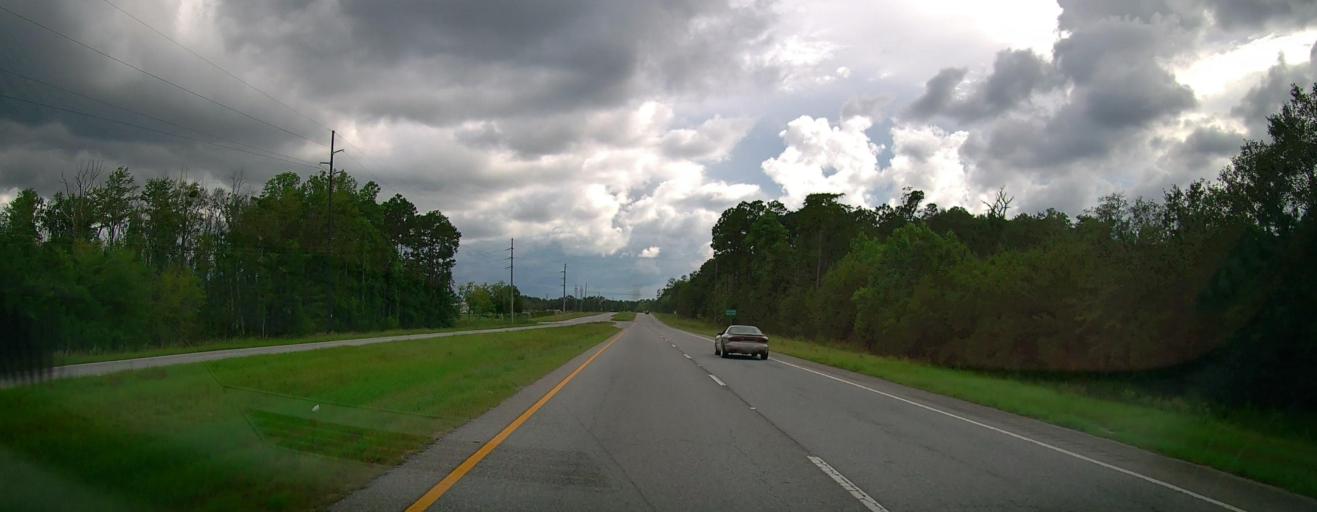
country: US
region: Georgia
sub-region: Pierce County
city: Blackshear
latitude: 31.4209
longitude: -82.1002
